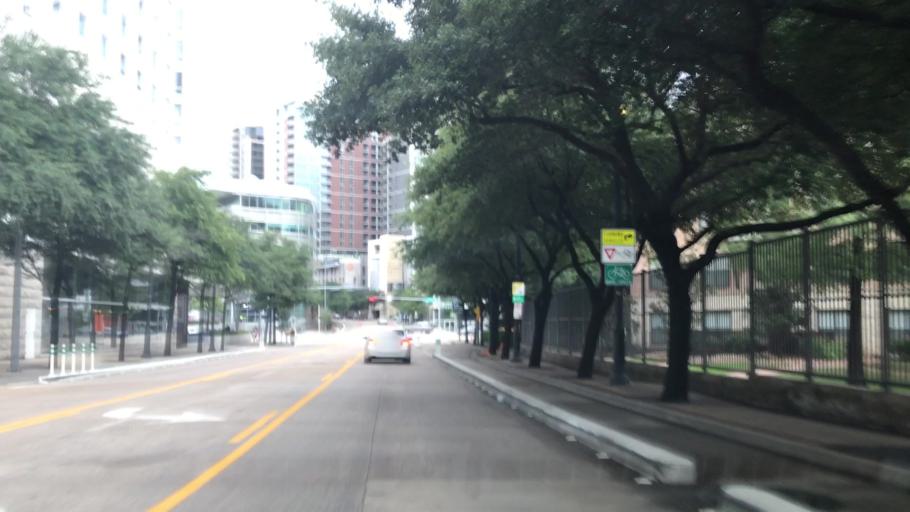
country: US
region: Texas
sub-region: Dallas County
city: Dallas
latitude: 32.7881
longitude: -96.8087
